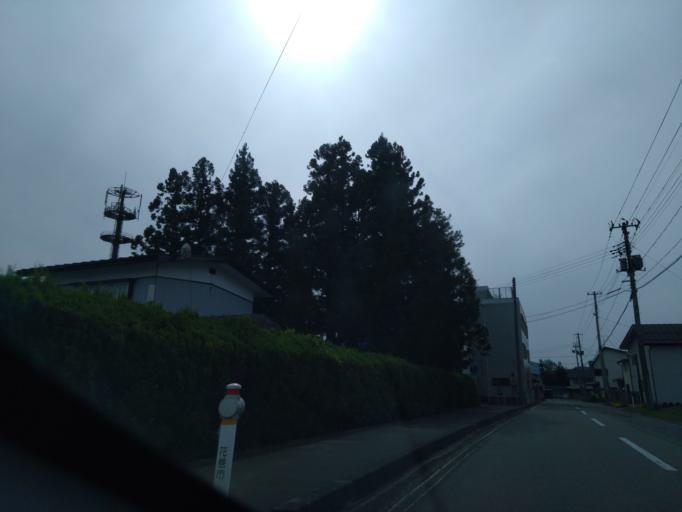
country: JP
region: Iwate
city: Hanamaki
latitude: 39.4384
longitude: 141.0804
